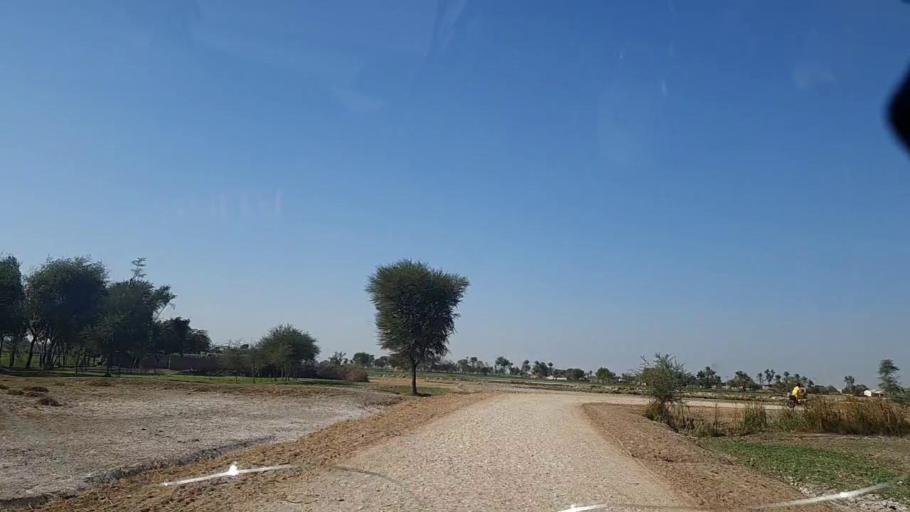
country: PK
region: Sindh
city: Khanpur
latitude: 27.8463
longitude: 69.3951
